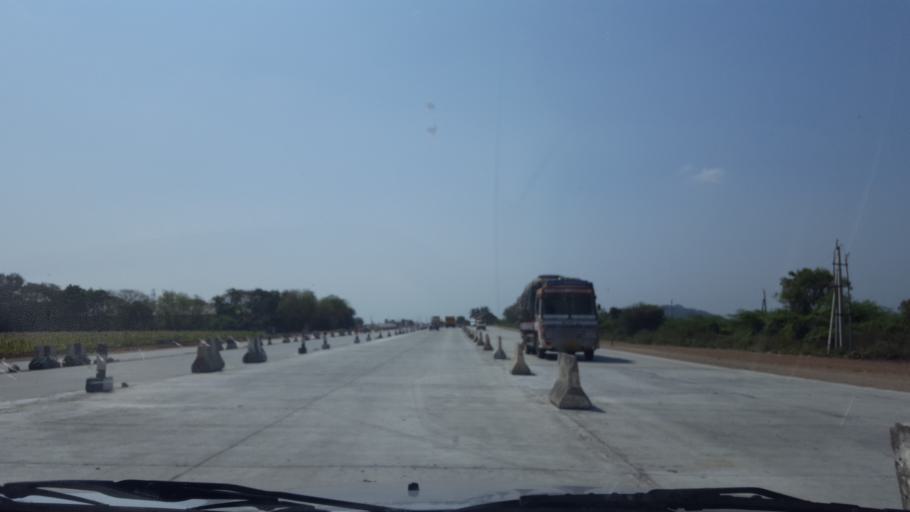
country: IN
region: Andhra Pradesh
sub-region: Prakasam
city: Addanki
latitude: 15.7627
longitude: 80.0324
